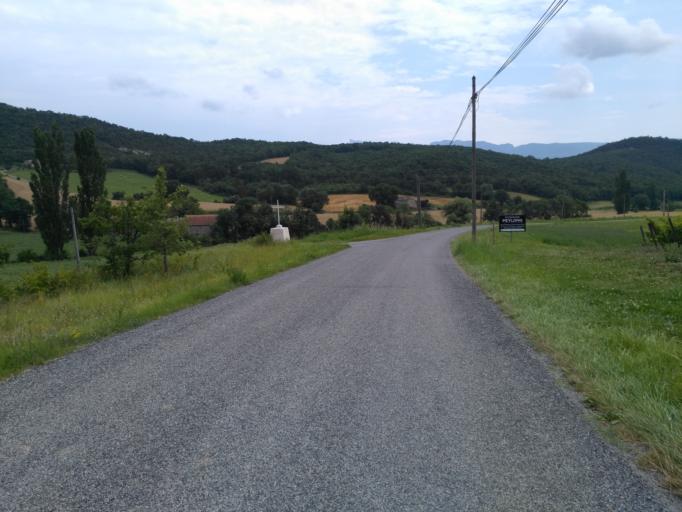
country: FR
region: Rhone-Alpes
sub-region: Departement de la Drome
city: Aouste-sur-Sye
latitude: 44.7563
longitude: 5.1168
